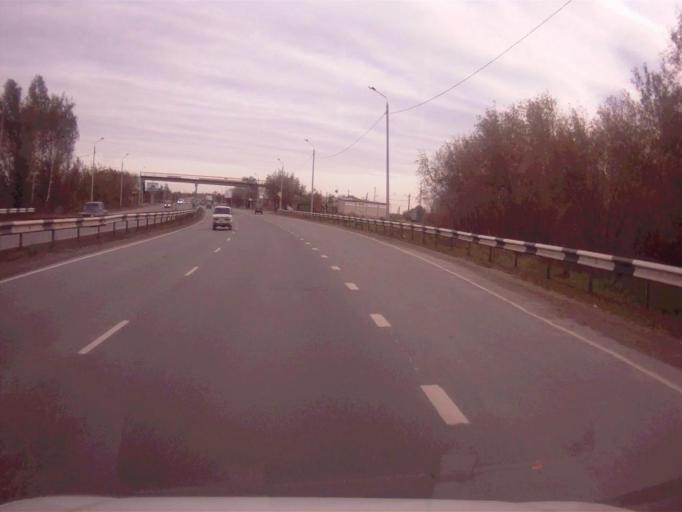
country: RU
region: Chelyabinsk
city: Novosineglazovskiy
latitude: 55.0430
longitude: 61.4254
